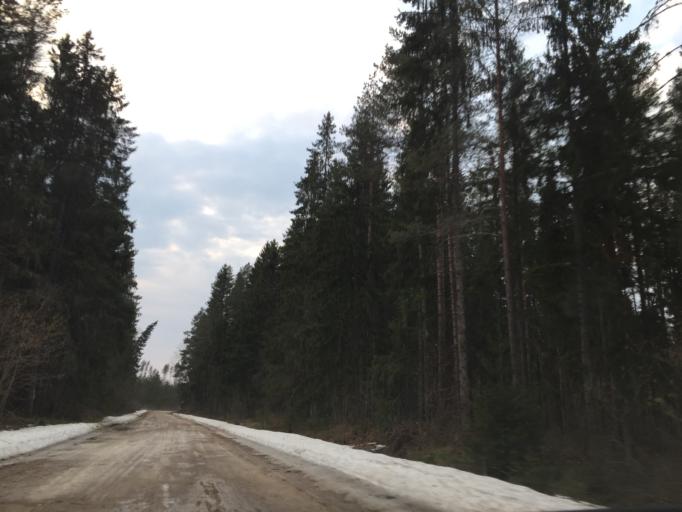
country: LV
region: Vecpiebalga
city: Vecpiebalga
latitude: 57.1347
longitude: 25.6360
